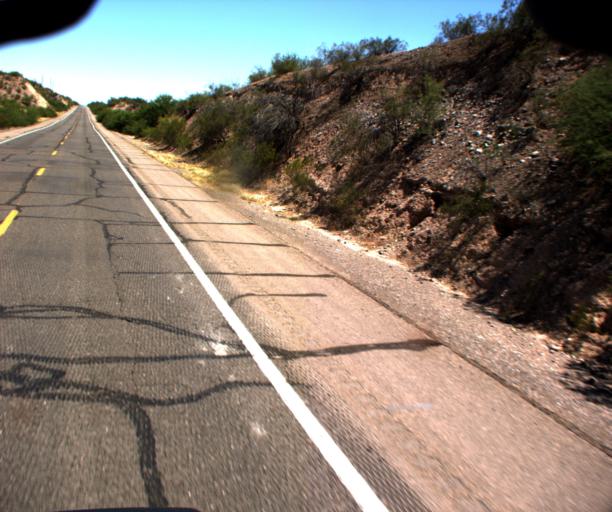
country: US
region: Arizona
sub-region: Pinal County
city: Mammoth
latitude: 32.7817
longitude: -110.6666
